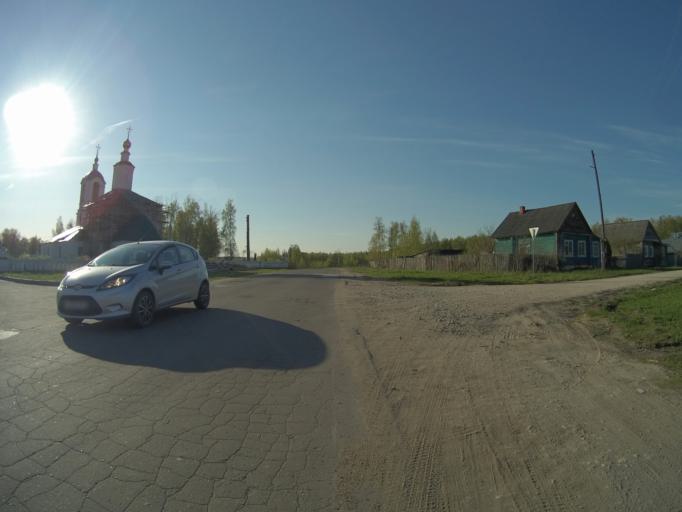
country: RU
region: Vladimir
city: Sudogda
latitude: 56.0729
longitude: 40.7872
